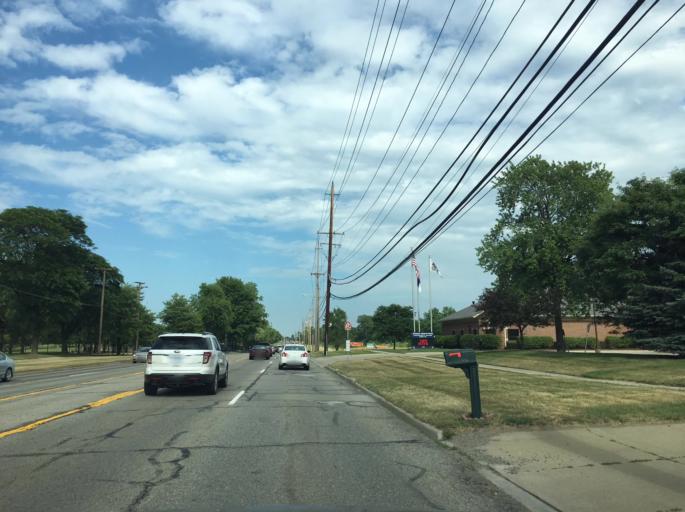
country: US
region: Michigan
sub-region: Macomb County
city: Sterling Heights
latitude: 42.5371
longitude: -83.0140
